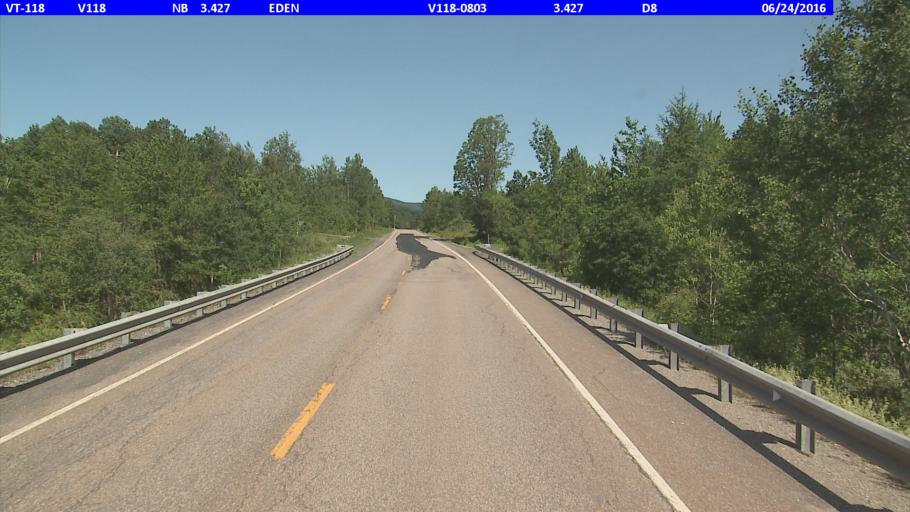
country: US
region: Vermont
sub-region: Lamoille County
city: Johnson
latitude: 44.7507
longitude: -72.5729
